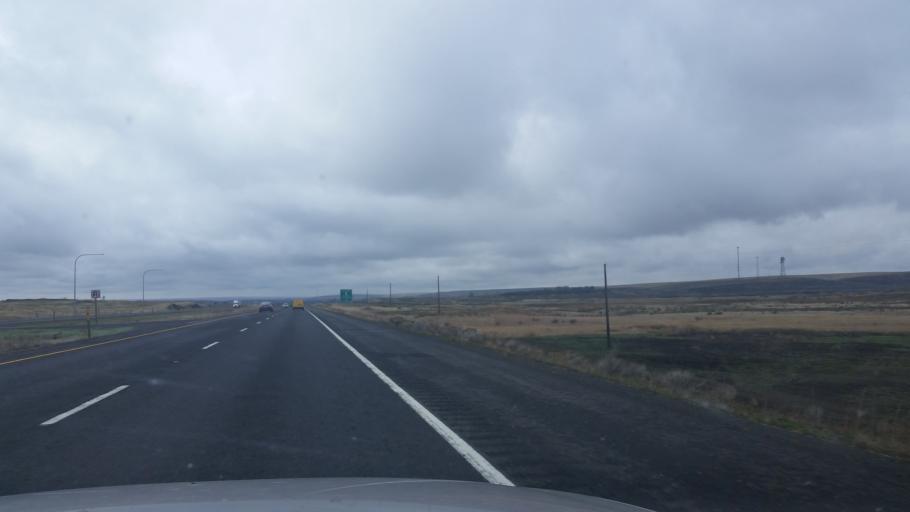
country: US
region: Washington
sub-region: Spokane County
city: Medical Lake
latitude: 47.3126
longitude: -117.9636
